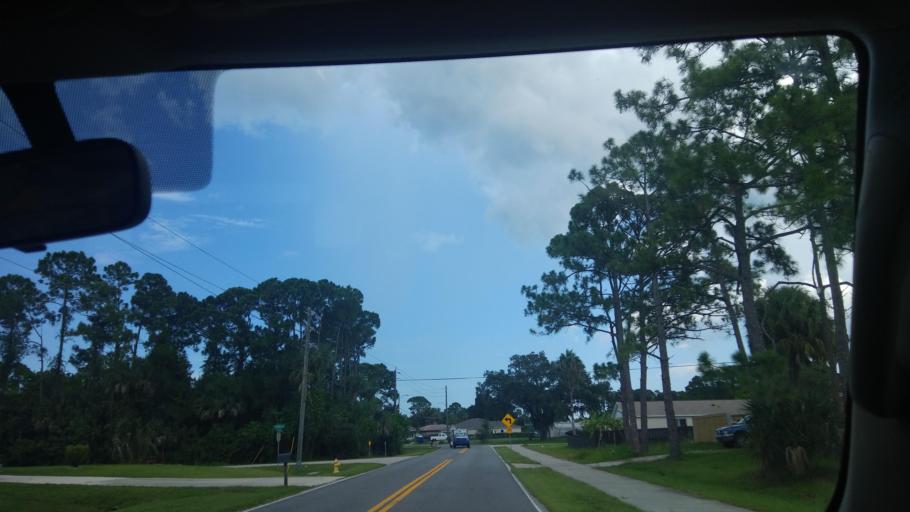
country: US
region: Florida
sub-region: Brevard County
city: West Melbourne
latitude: 28.0100
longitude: -80.6618
